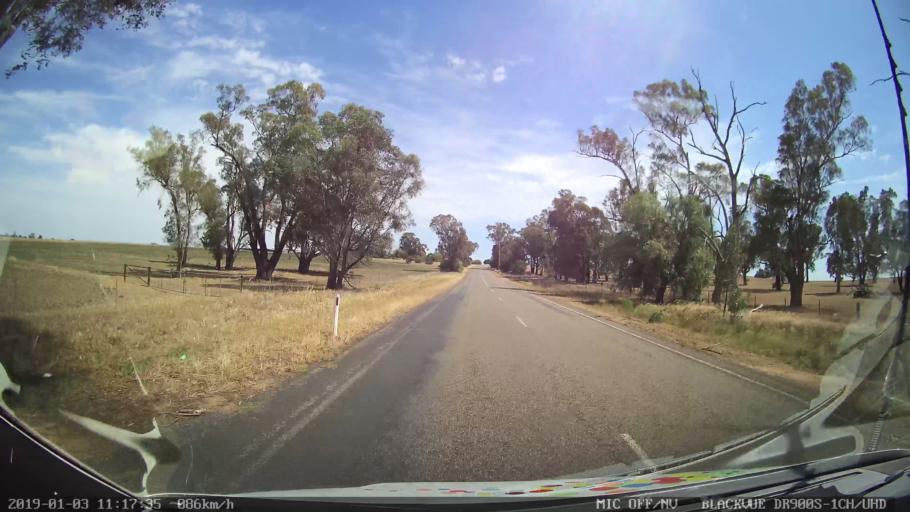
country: AU
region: New South Wales
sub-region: Young
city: Young
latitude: -34.1368
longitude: 148.2653
